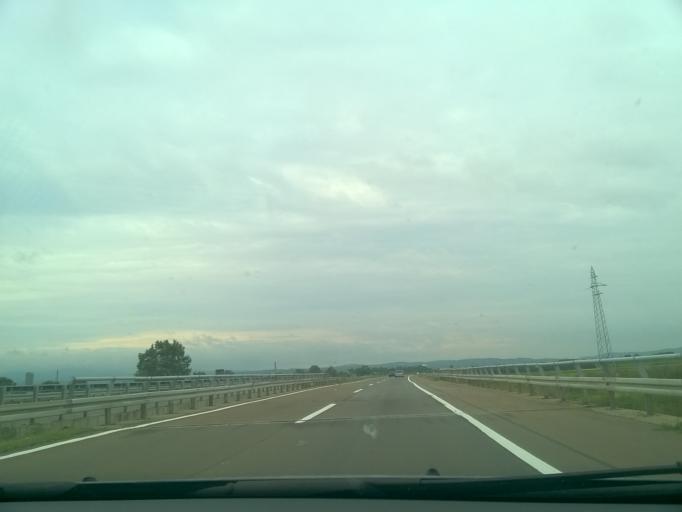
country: RS
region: Central Serbia
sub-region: Pomoravski Okrug
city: Jagodina
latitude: 43.9776
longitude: 21.2871
